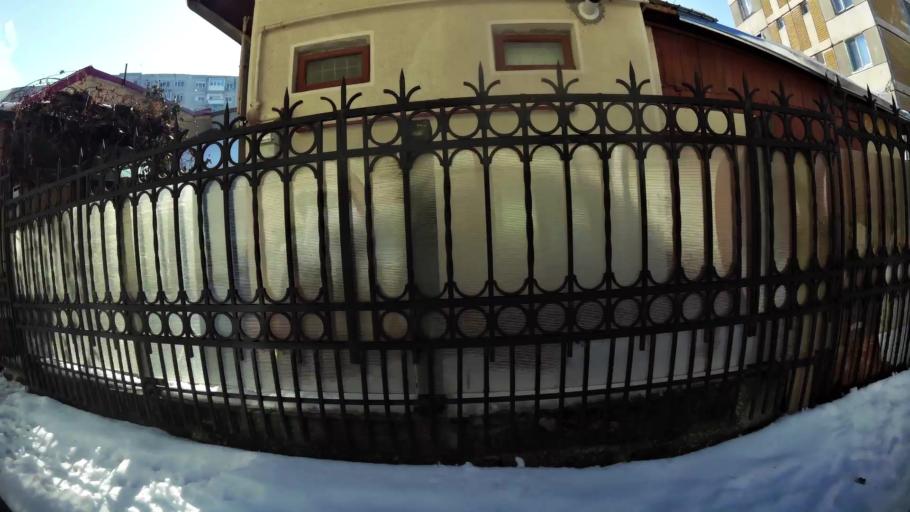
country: RO
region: Bucuresti
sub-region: Municipiul Bucuresti
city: Bucuresti
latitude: 44.4054
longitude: 26.0599
